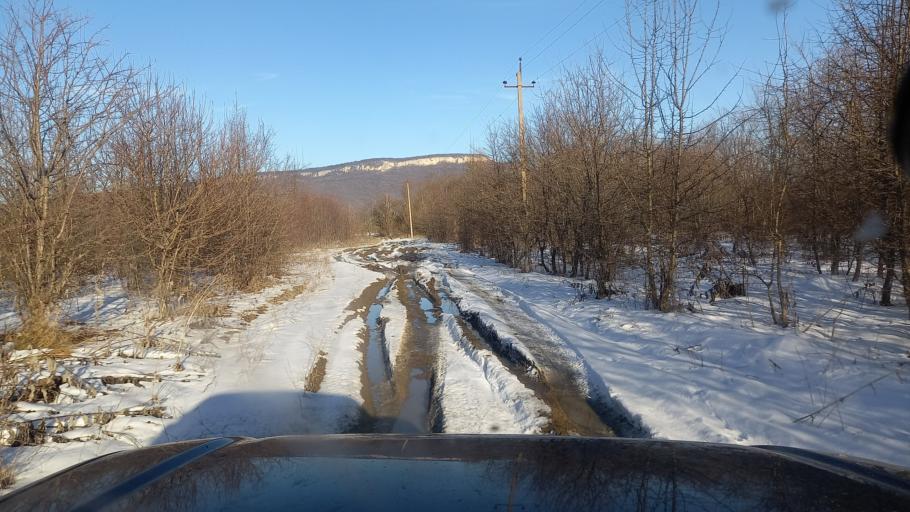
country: RU
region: Adygeya
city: Kamennomostskiy
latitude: 44.2147
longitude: 40.1717
